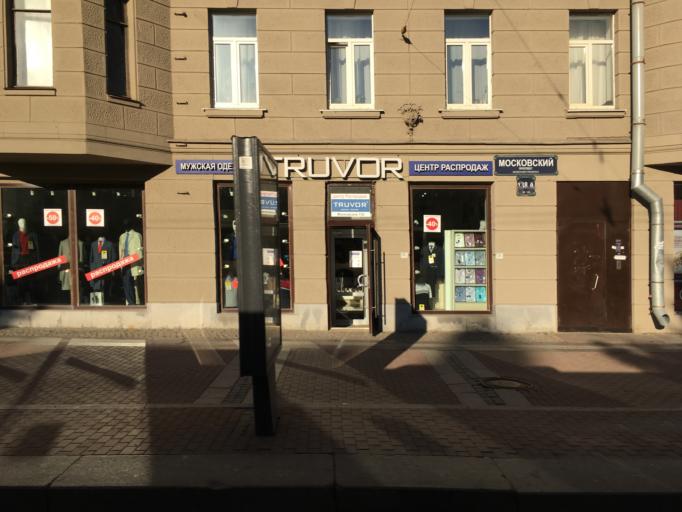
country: RU
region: St.-Petersburg
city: Admiralteisky
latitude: 59.8866
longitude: 30.3202
